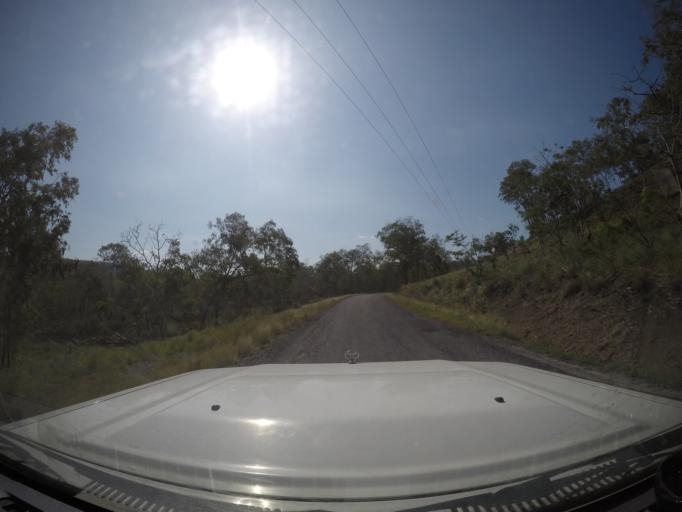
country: PG
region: Central Province
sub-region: Rigo
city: Kwikila
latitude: -9.8717
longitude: 147.5660
